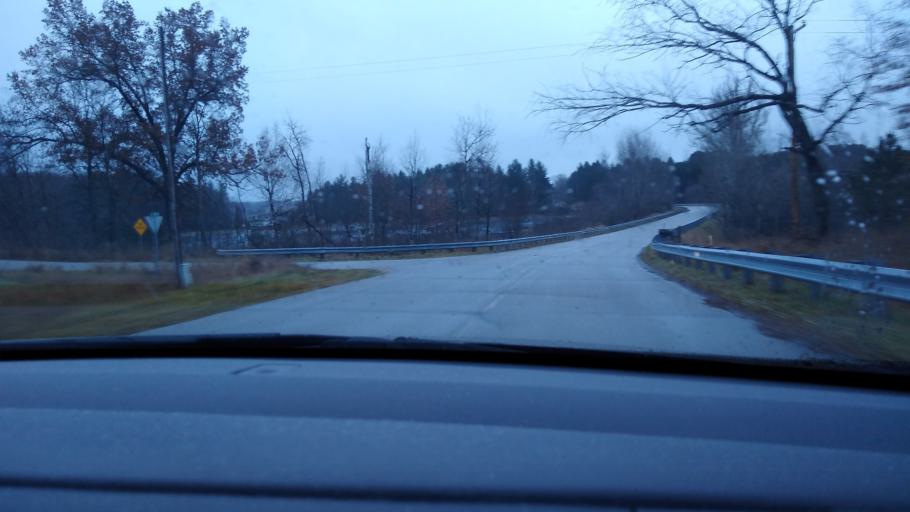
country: US
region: Michigan
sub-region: Wexford County
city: Cadillac
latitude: 44.1871
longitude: -85.3954
